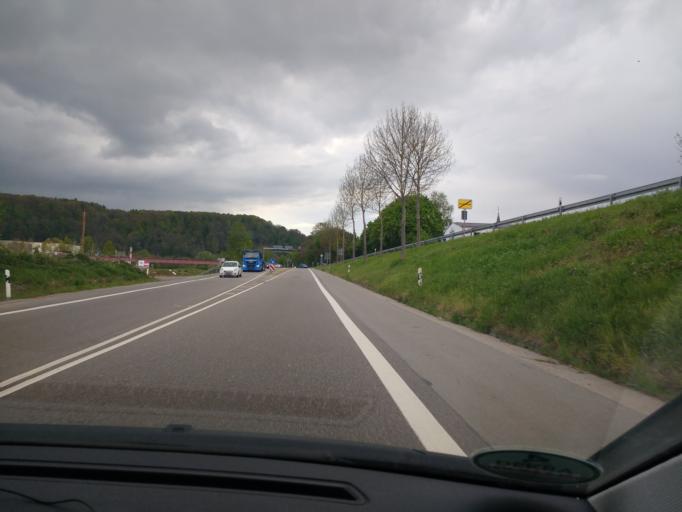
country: FR
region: Lorraine
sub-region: Departement de la Moselle
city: Alsting
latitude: 49.1974
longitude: 7.0289
